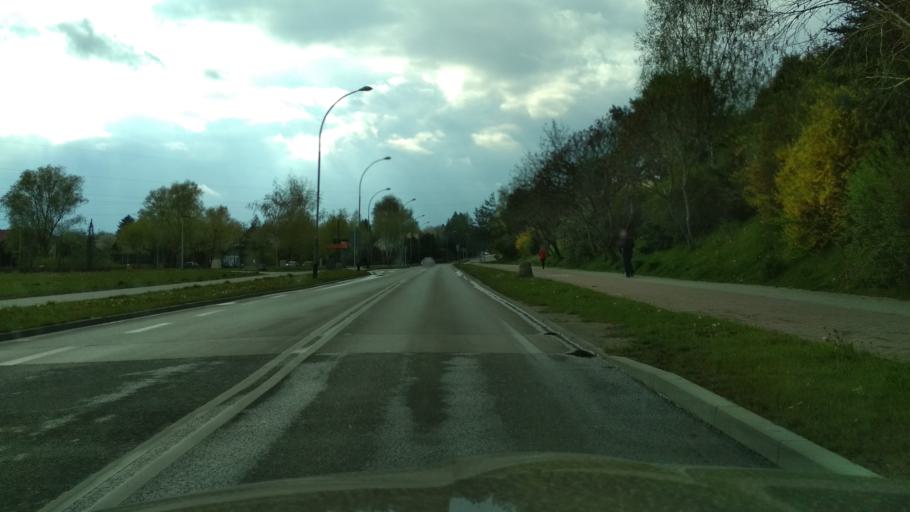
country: PL
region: Subcarpathian Voivodeship
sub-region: Rzeszow
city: Rzeszow
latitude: 50.0410
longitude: 21.9745
